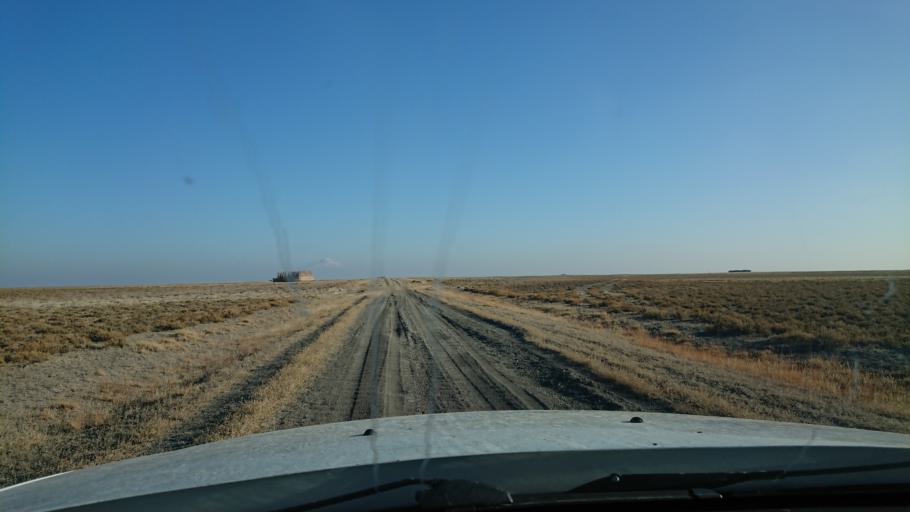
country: TR
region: Aksaray
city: Sultanhani
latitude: 38.3951
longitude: 33.5912
